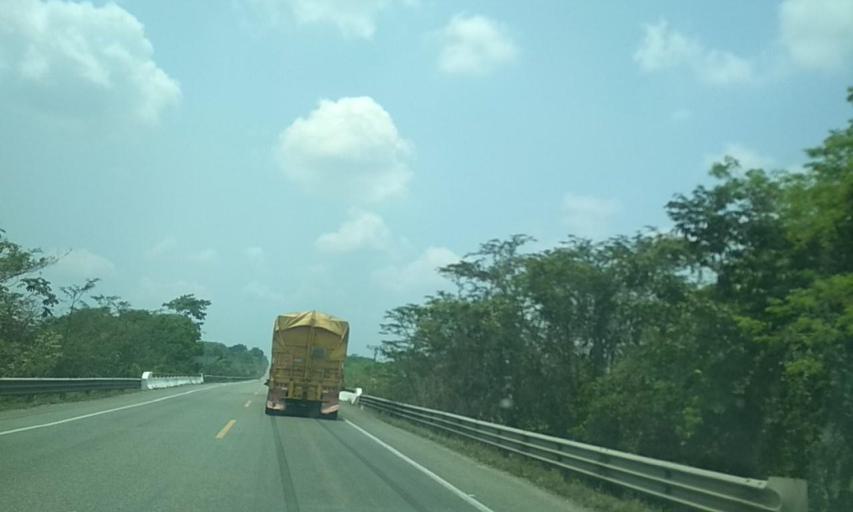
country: MX
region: Tabasco
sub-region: Huimanguillo
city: Francisco Rueda
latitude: 17.7367
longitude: -93.9760
